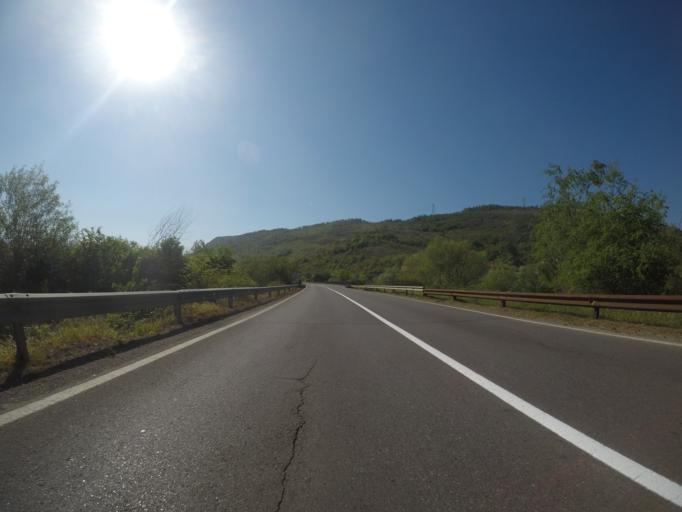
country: ME
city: Spuz
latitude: 42.4616
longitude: 19.1767
